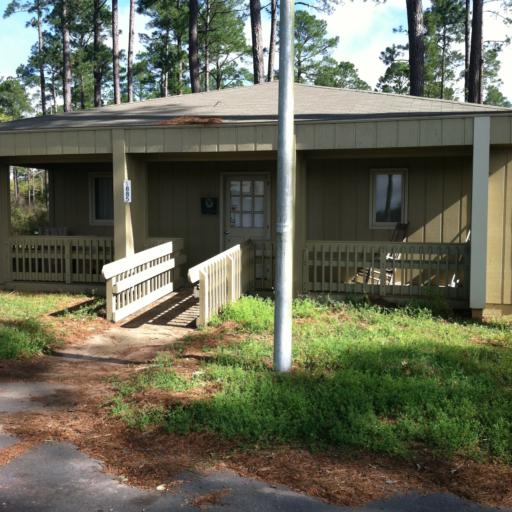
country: US
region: Georgia
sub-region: Early County
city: Blakely
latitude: 31.4694
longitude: -84.9217
